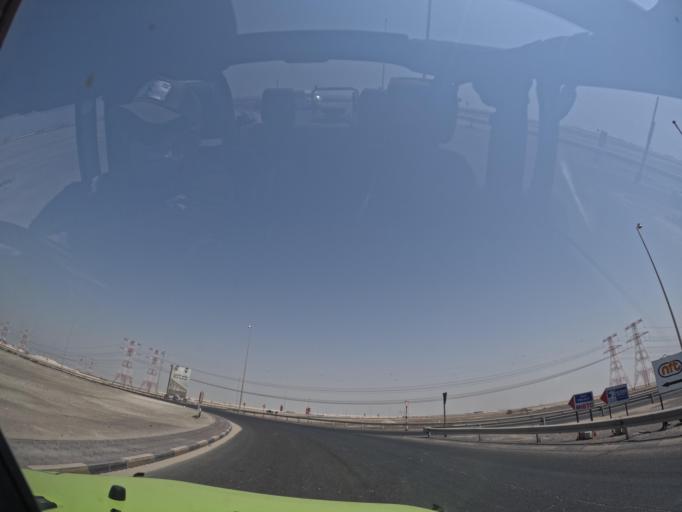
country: AE
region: Abu Dhabi
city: Abu Dhabi
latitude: 24.2024
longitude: 54.4205
